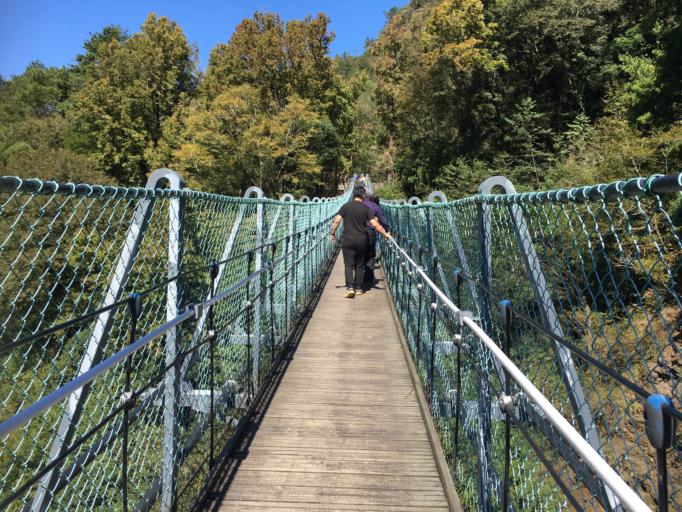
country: TW
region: Taiwan
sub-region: Nantou
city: Puli
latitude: 23.9454
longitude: 121.1910
